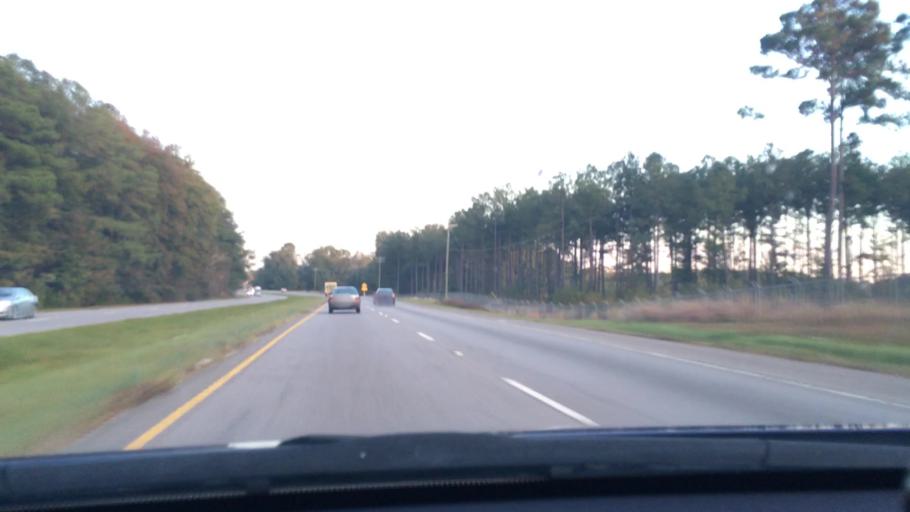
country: US
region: South Carolina
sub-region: Richland County
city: Hopkins
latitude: 33.9392
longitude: -80.7926
